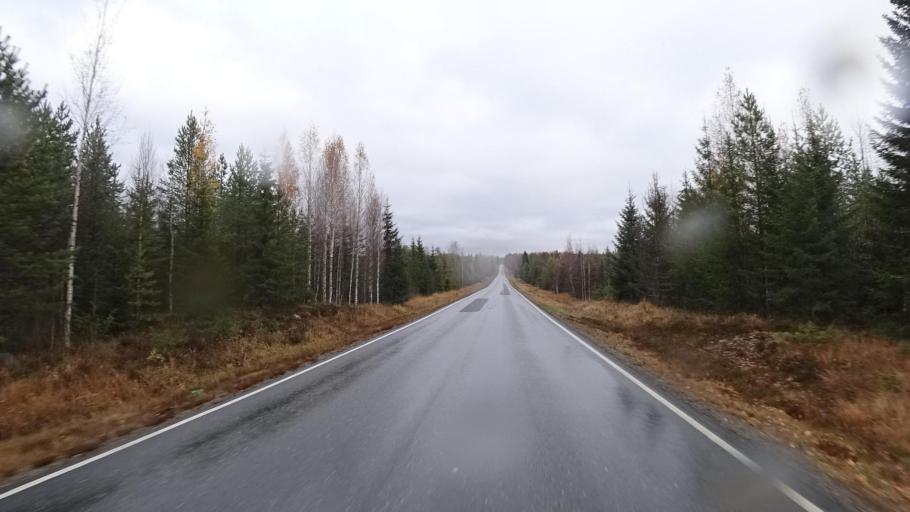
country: FI
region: North Karelia
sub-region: Joensuu
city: Polvijaervi
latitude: 63.0866
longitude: 29.5895
